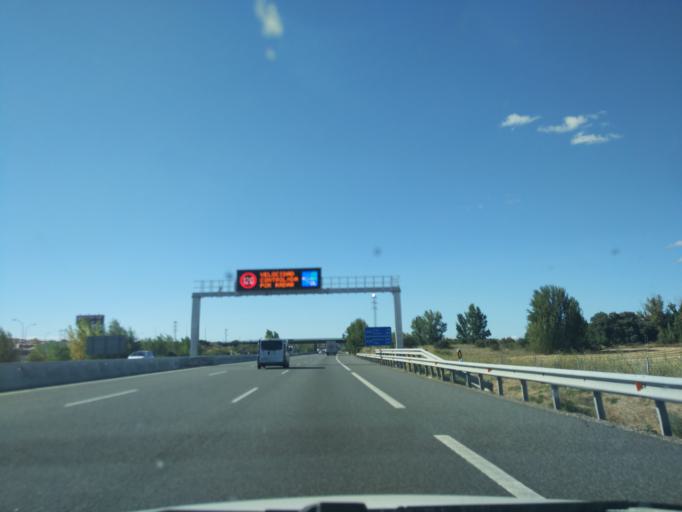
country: ES
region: Castille and Leon
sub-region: Provincia de Zamora
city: Benavente
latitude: 42.0056
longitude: -5.6608
